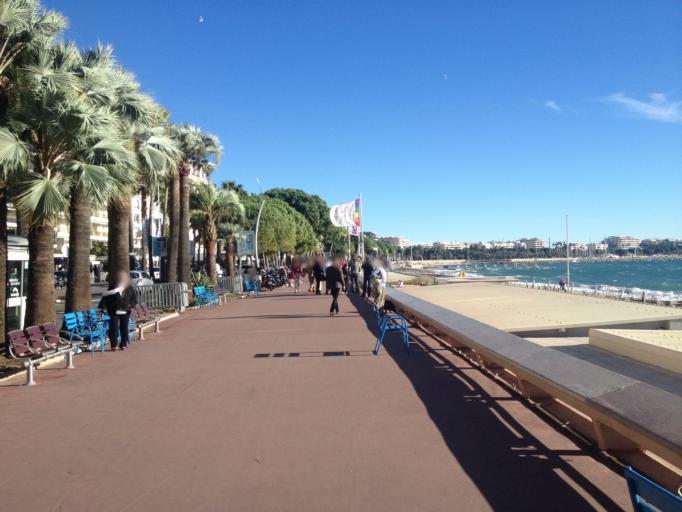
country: FR
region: Provence-Alpes-Cote d'Azur
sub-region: Departement des Alpes-Maritimes
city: Cannes
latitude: 43.5491
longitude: 7.0270
